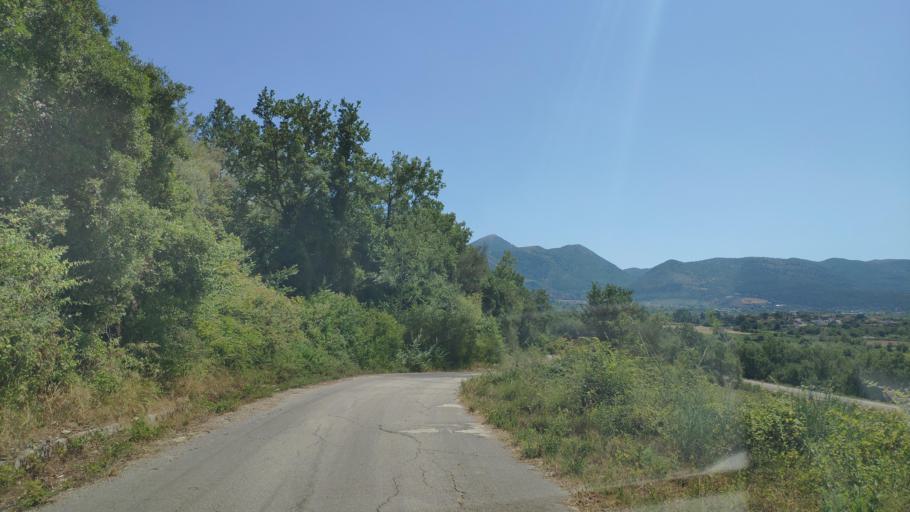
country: GR
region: Epirus
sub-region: Nomos Prevezis
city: Kanalaki
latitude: 39.2704
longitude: 20.6004
